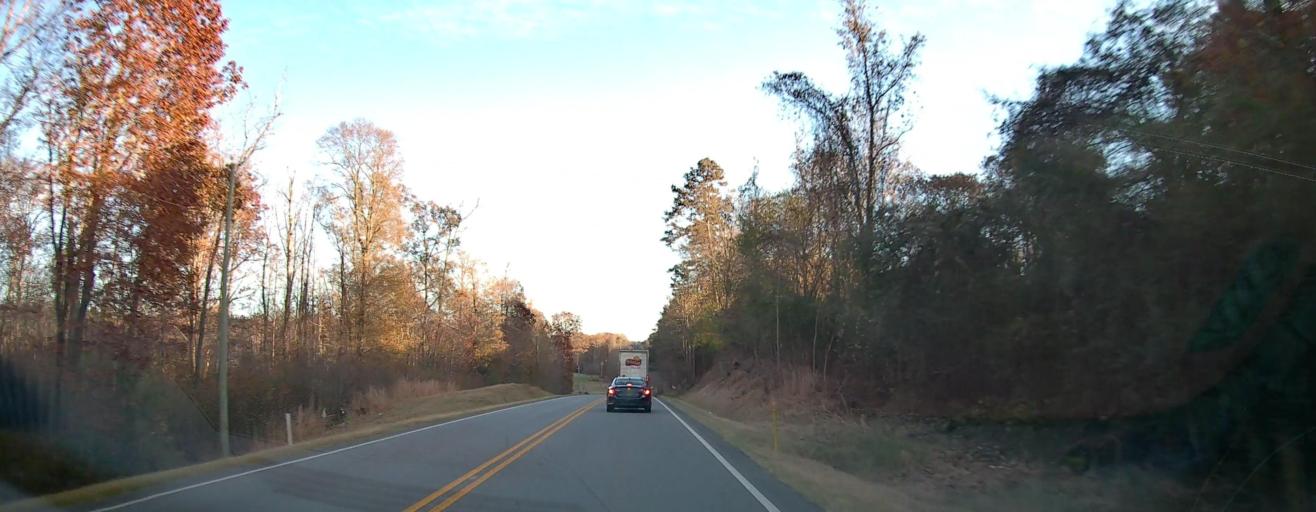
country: US
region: Alabama
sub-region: Blount County
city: Oneonta
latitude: 34.0892
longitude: -86.3504
